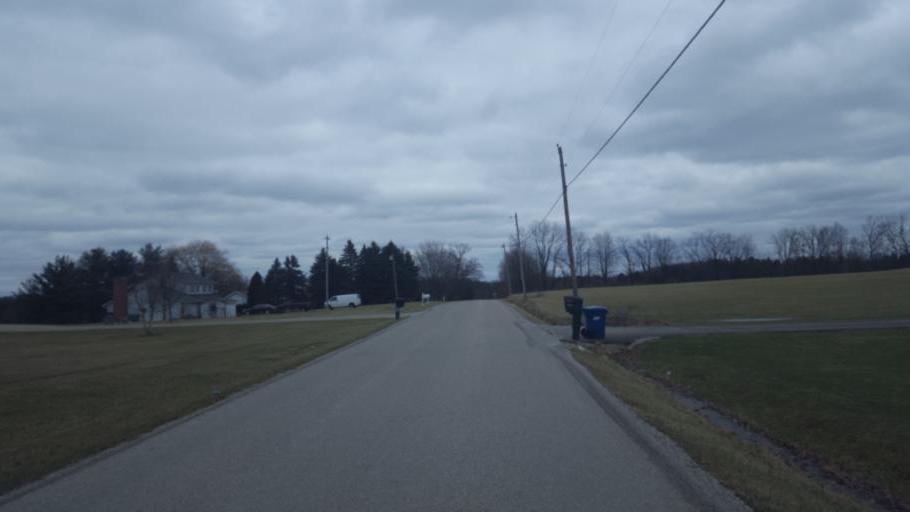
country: US
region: Ohio
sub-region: Richland County
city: Ontario
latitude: 40.7364
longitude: -82.5951
